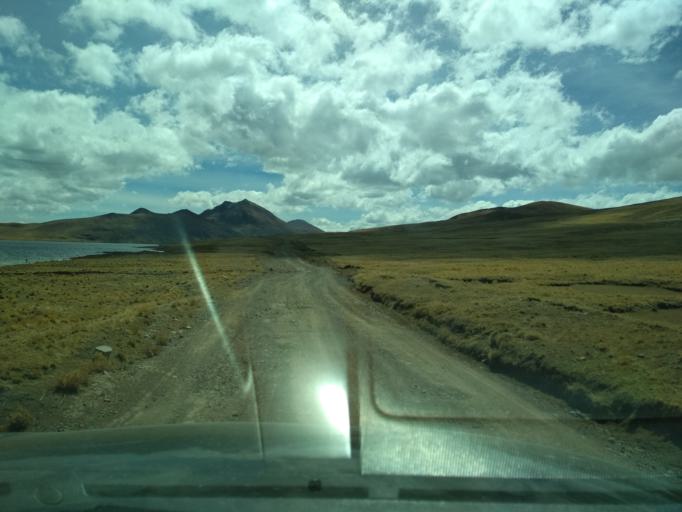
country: PE
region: Huancavelica
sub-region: Provincia de Huancavelica
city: Acobambilla
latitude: -12.7206
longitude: -75.5085
